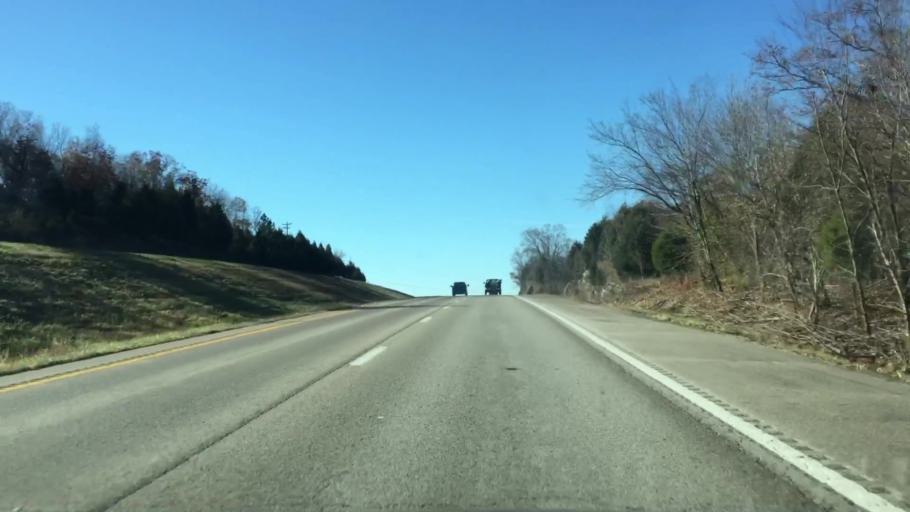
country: US
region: Missouri
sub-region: Cole County
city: Wardsville
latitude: 38.5146
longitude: -92.2396
